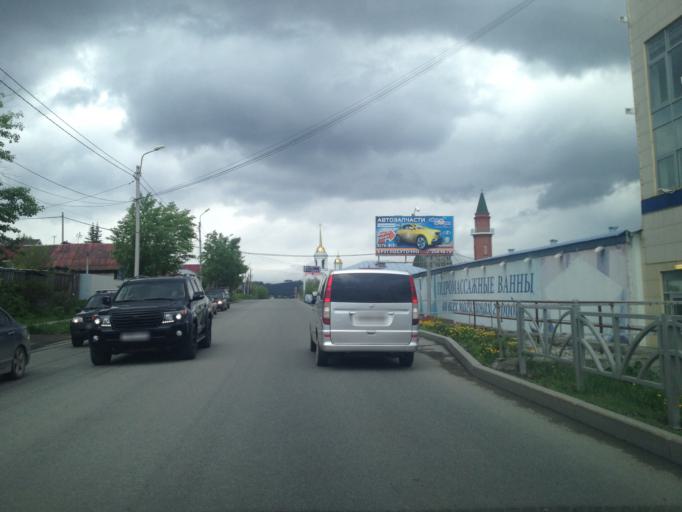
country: RU
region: Sverdlovsk
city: Istok
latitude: 56.7444
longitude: 60.6942
